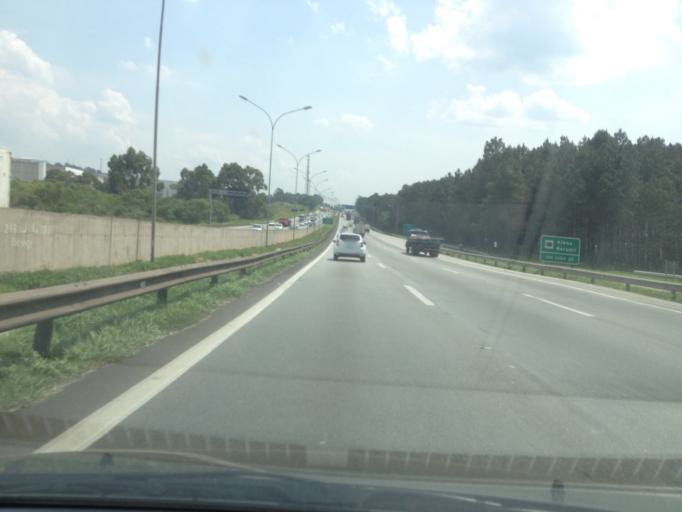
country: BR
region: Sao Paulo
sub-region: Jandira
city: Jandira
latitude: -23.5117
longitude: -46.9162
